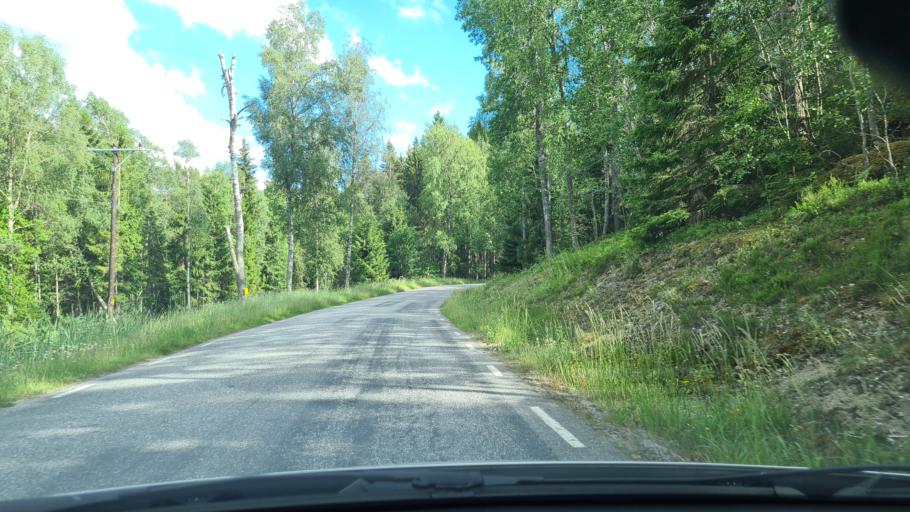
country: SE
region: Stockholm
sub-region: Varmdo Kommun
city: Mortnas
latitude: 59.4022
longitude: 18.4616
